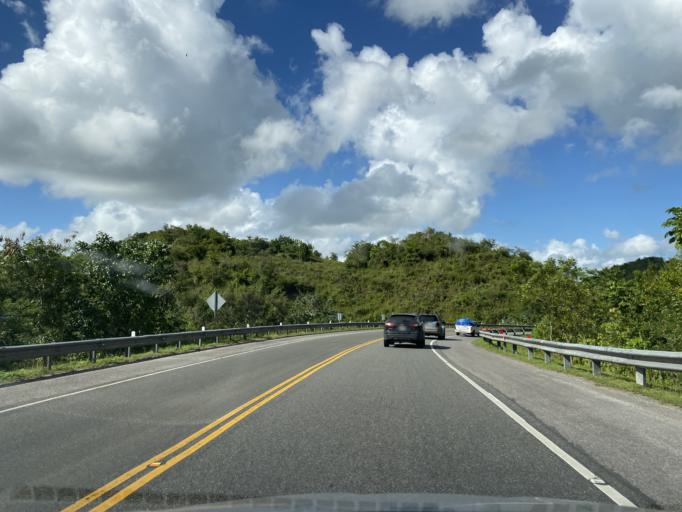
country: DO
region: Duarte
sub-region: Villa Riva
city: Agua Santa del Yuna
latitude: 19.1018
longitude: -69.8311
